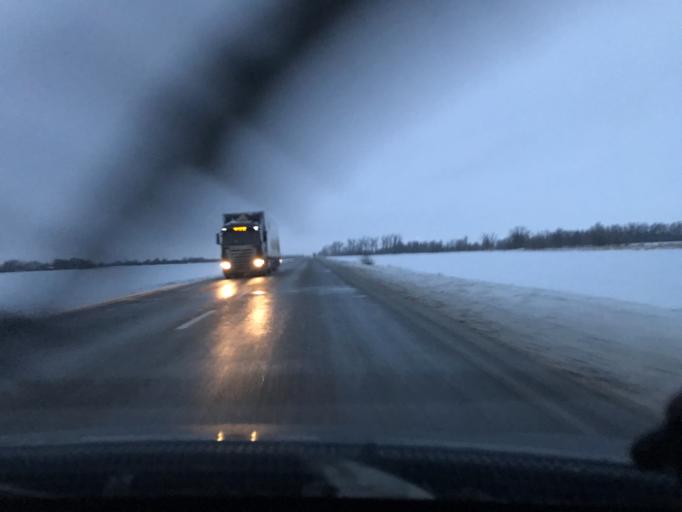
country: RU
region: Rostov
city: Letnik
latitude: 45.9387
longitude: 41.2882
